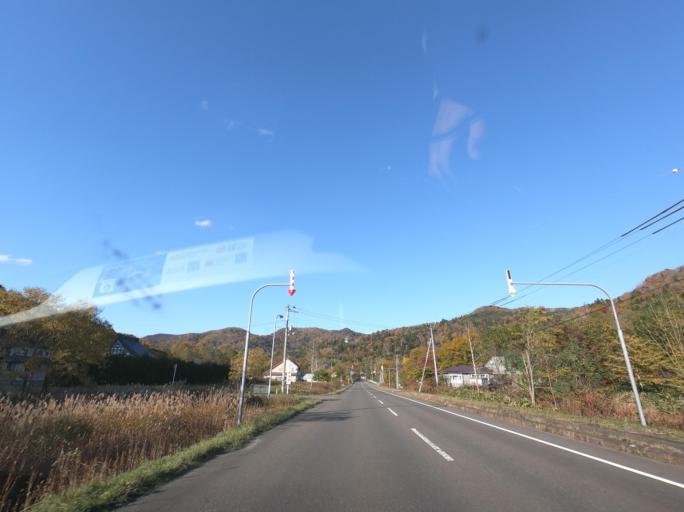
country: JP
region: Hokkaido
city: Iwamizawa
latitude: 43.0032
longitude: 142.0053
